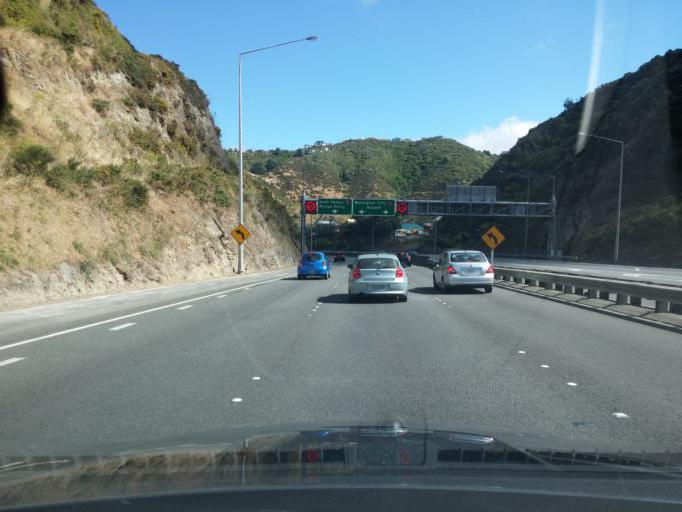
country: NZ
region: Wellington
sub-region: Wellington City
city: Wellington
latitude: -41.2345
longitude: 174.8068
